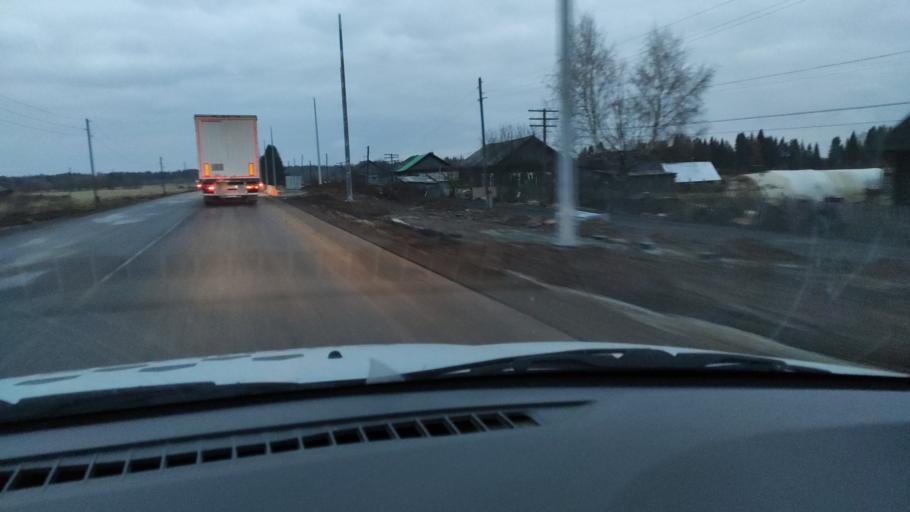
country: RU
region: Kirov
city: Kostino
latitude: 58.8306
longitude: 53.3079
